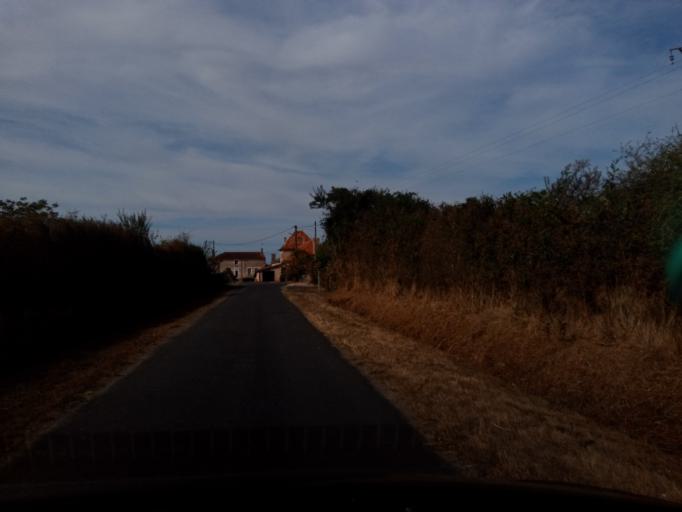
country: FR
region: Poitou-Charentes
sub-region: Departement de la Vienne
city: Montmorillon
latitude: 46.4065
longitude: 0.8699
